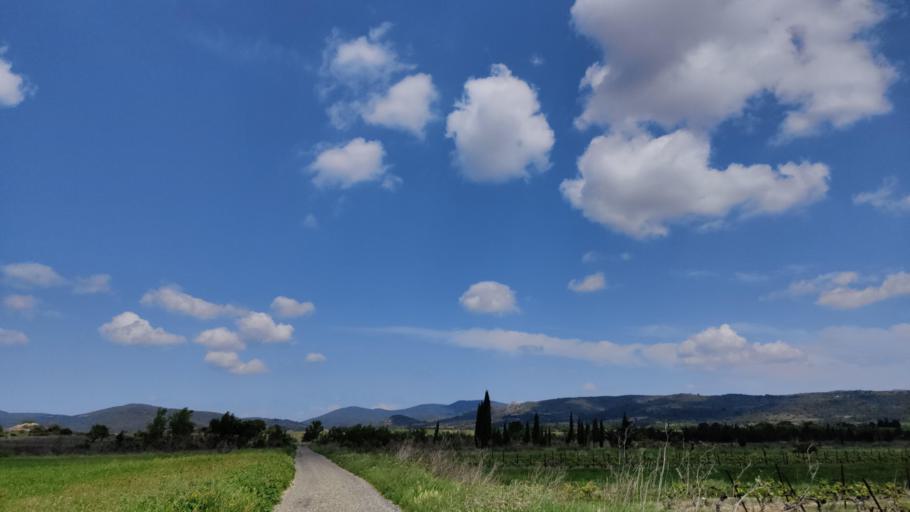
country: FR
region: Languedoc-Roussillon
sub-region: Departement des Pyrenees-Orientales
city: Estagel
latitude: 42.8694
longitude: 2.7195
